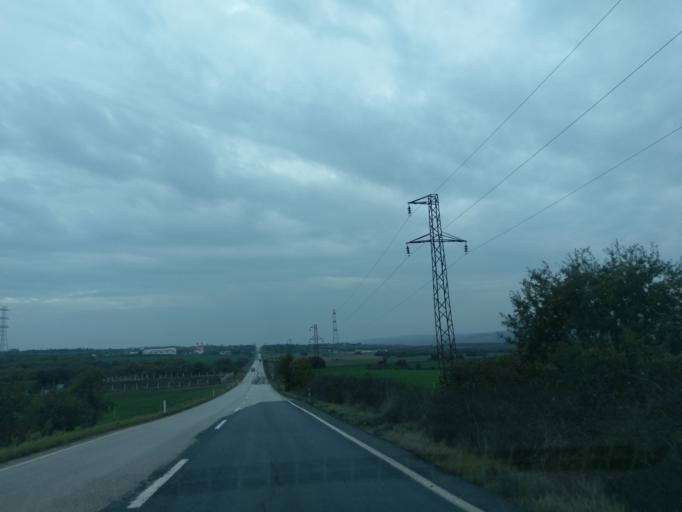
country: TR
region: Istanbul
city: Canta
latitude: 41.1519
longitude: 28.1068
